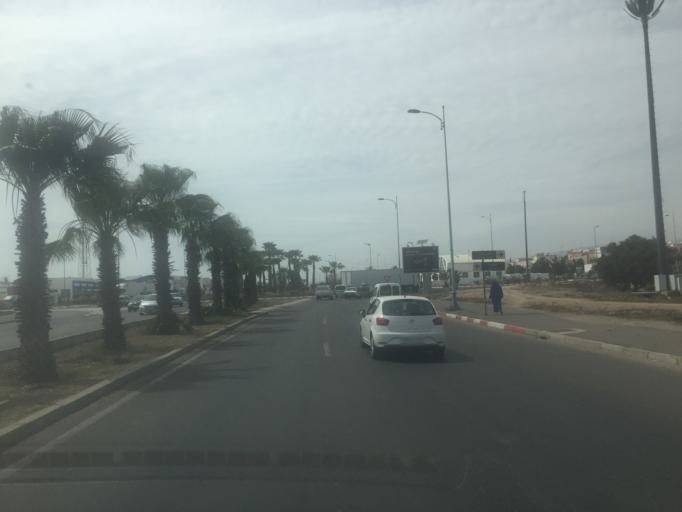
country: MA
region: Souss-Massa-Draa
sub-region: Inezgane-Ait Mellou
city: Inezgane
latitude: 30.3886
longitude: -9.5121
